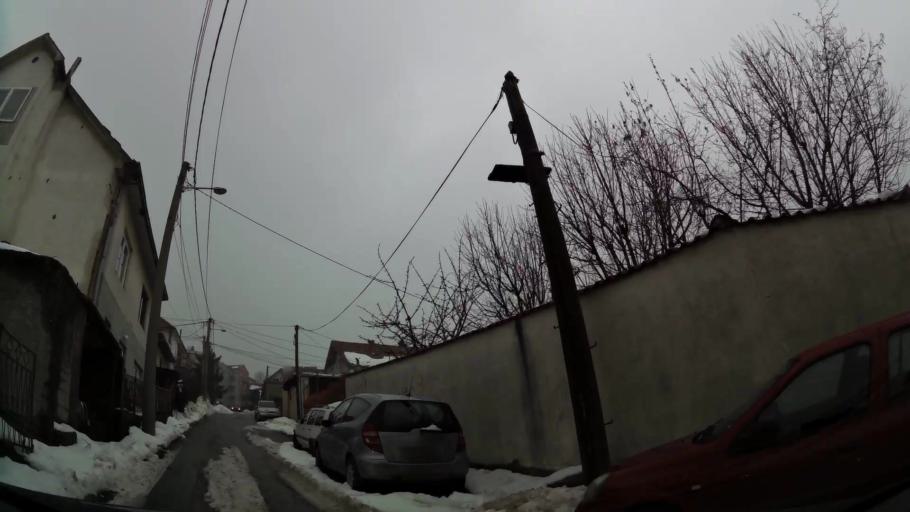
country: RS
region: Central Serbia
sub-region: Belgrade
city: Zvezdara
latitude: 44.7871
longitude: 20.5243
